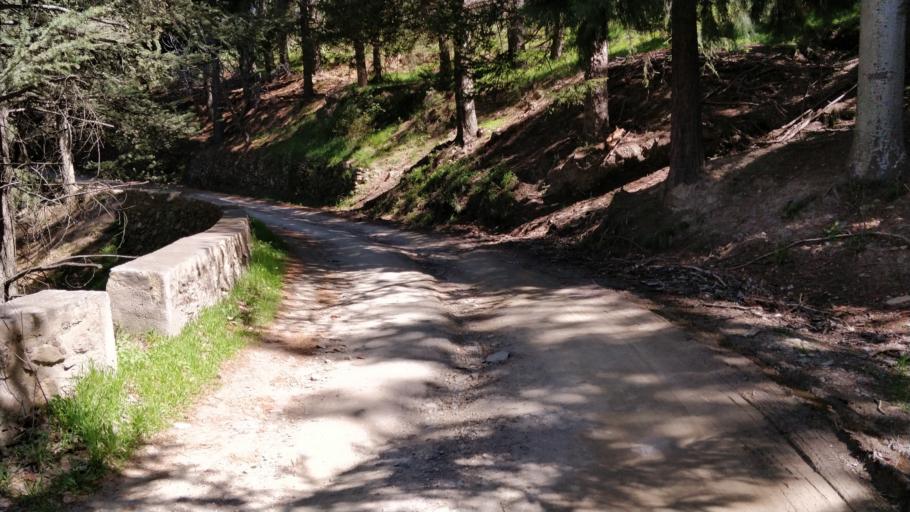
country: ES
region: Andalusia
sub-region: Provincia de Granada
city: Soportujar
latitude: 36.9404
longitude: -3.4060
